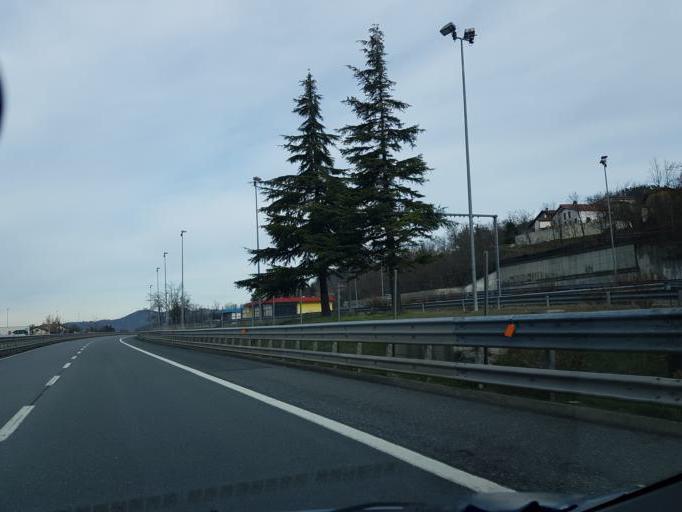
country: IT
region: Piedmont
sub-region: Provincia di Alessandria
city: Arquata Scrivia
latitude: 44.6700
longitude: 8.9067
